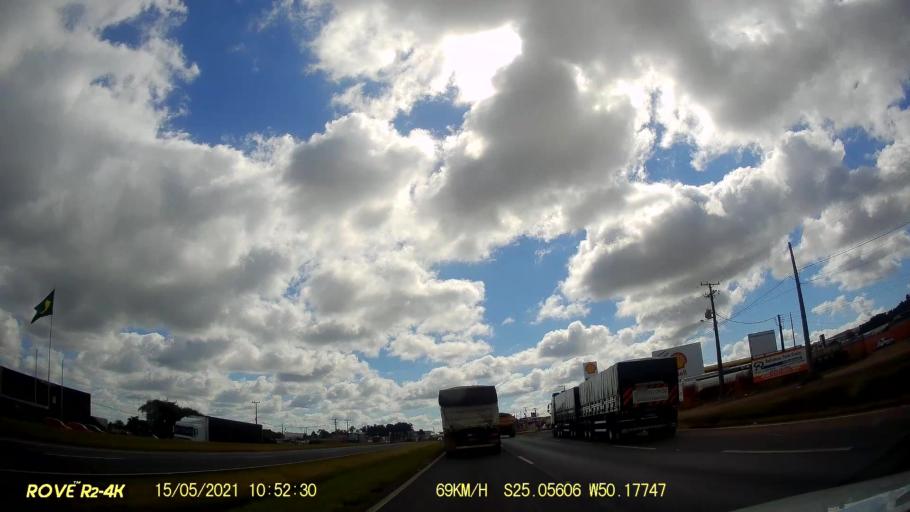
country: BR
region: Parana
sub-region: Ponta Grossa
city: Ponta Grossa
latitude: -25.0561
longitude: -50.1775
